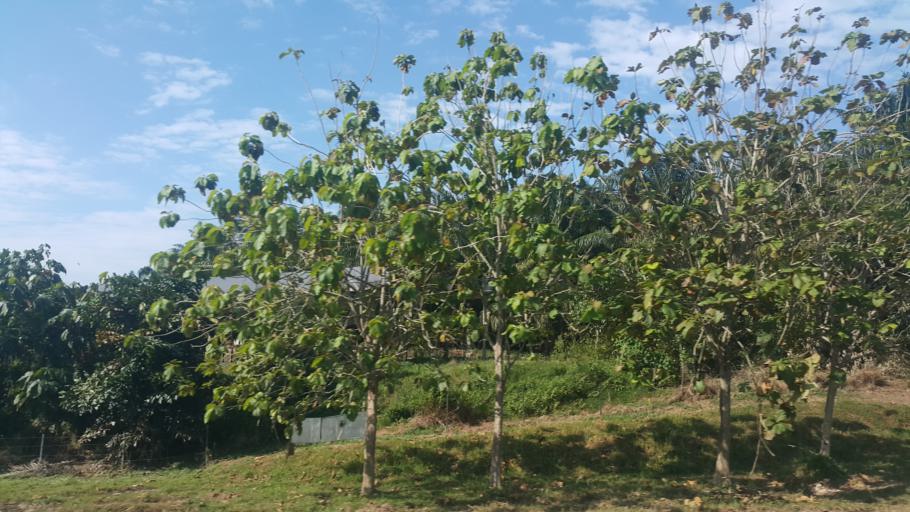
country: MY
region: Johor
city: Kelapa Sawit
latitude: 1.7261
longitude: 103.4275
